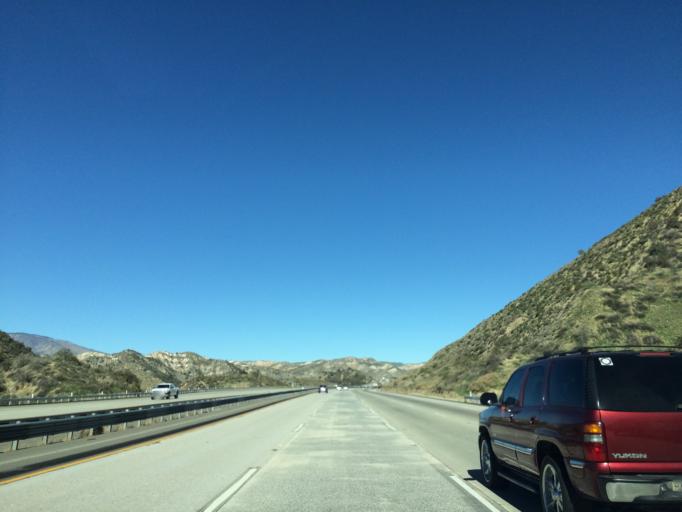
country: US
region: California
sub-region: Kern County
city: Lebec
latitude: 34.6955
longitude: -118.7908
